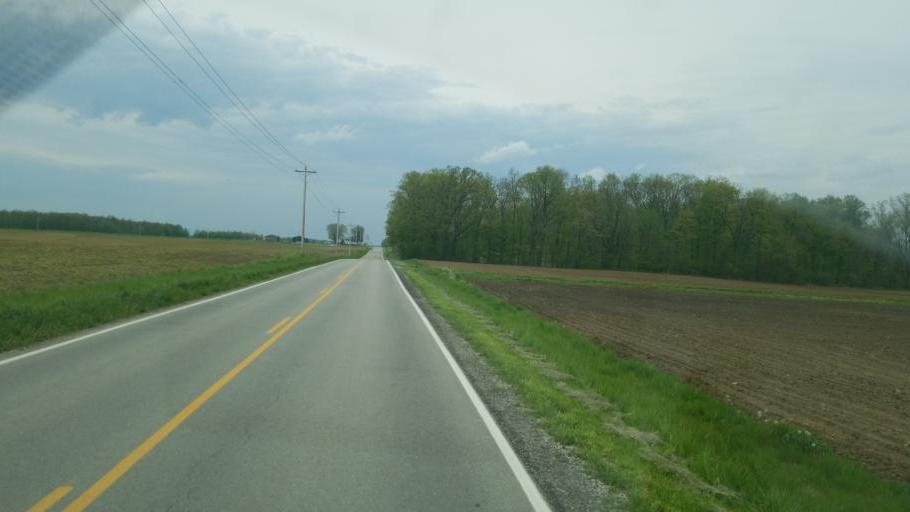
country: US
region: Ohio
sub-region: Huron County
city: Plymouth
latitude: 40.9565
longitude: -82.7433
